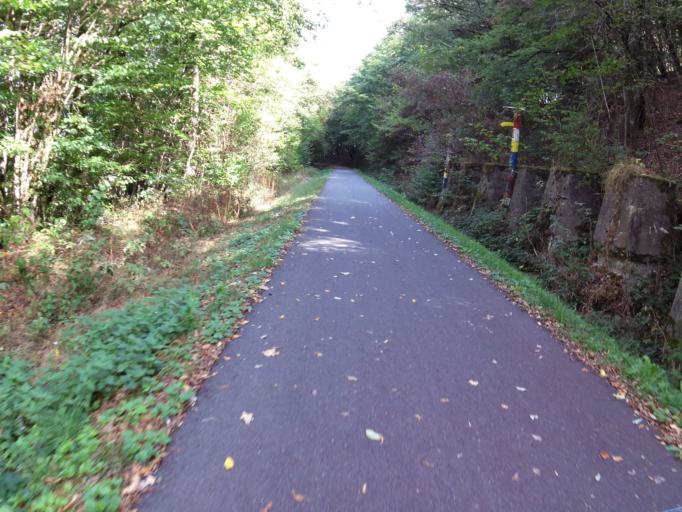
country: DE
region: Rheinland-Pfalz
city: Arzfeld
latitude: 50.0865
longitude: 6.2775
